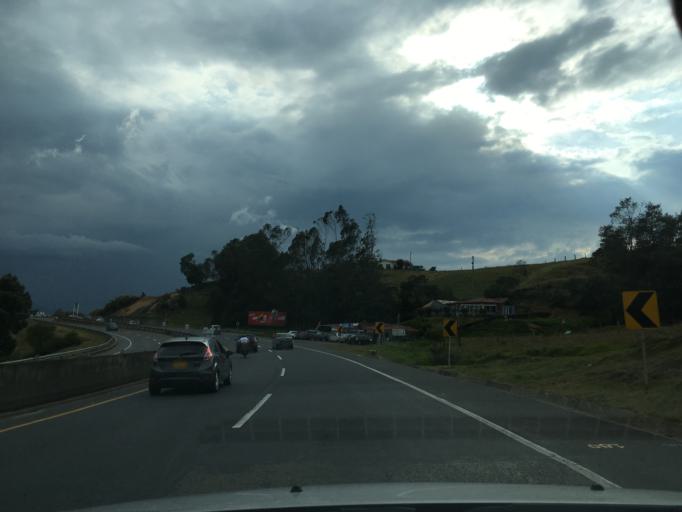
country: CO
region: Boyaca
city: Ventaquemada
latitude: 5.4082
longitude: -73.4752
